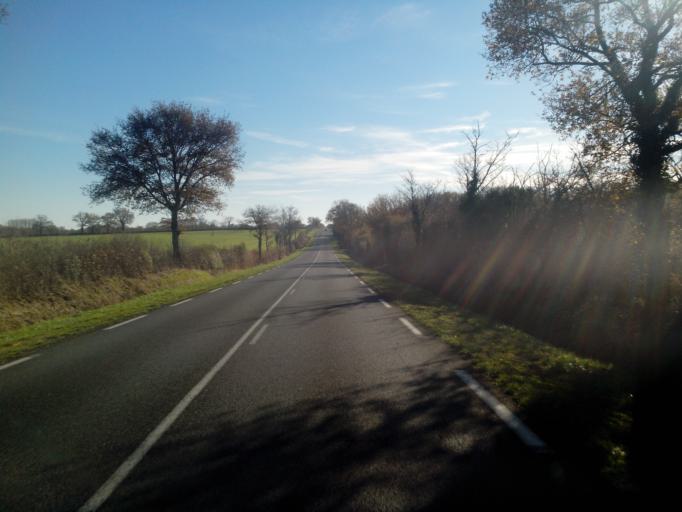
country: FR
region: Limousin
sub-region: Departement de la Haute-Vienne
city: Bussiere-Poitevine
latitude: 46.2943
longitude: 0.8430
